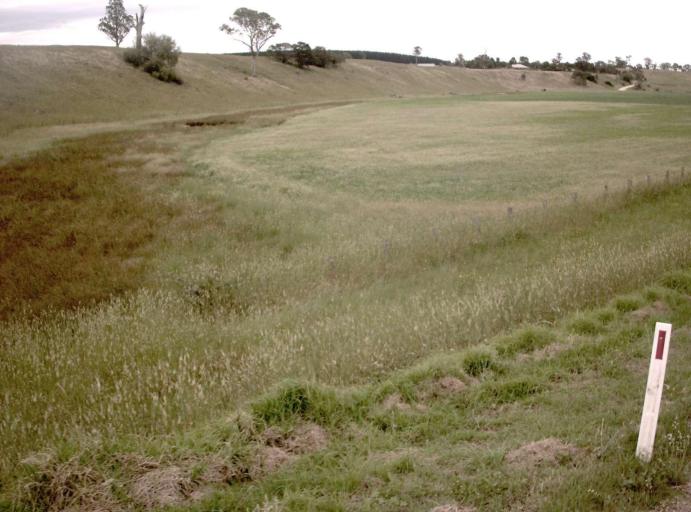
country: AU
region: Victoria
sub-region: East Gippsland
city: Bairnsdale
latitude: -37.7969
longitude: 147.4301
